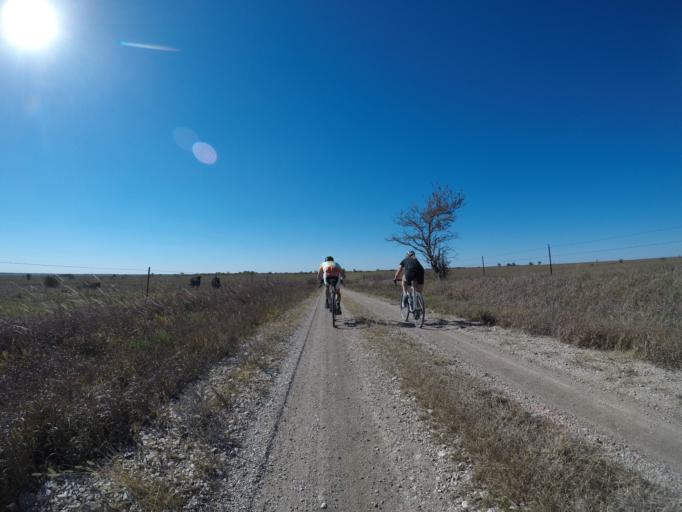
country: US
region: Kansas
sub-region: Wabaunsee County
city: Alma
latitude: 38.9711
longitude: -96.4573
